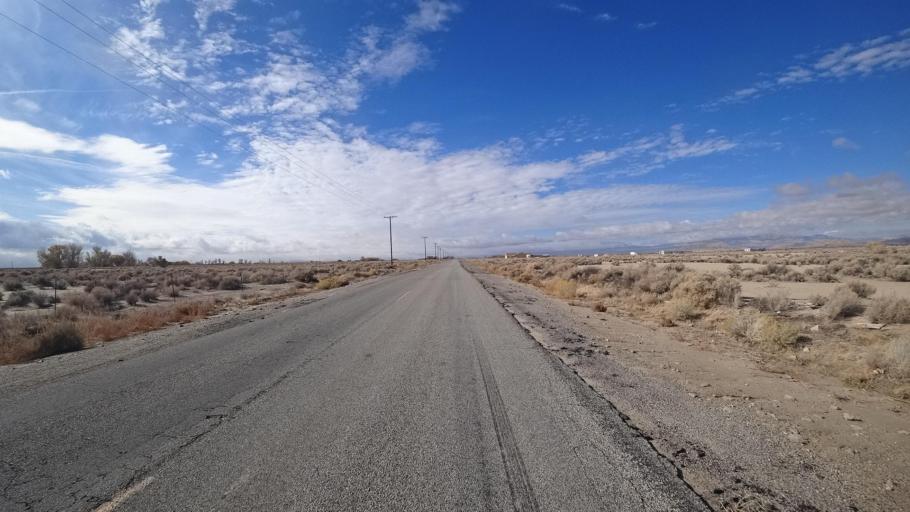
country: US
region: California
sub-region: Kern County
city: Rosamond
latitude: 34.8204
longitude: -118.1768
